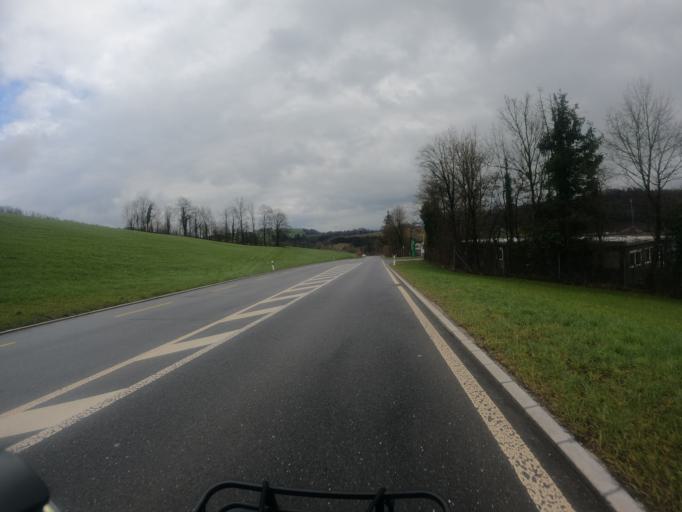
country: CH
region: Zurich
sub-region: Bezirk Affoltern
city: Hausen am Albis / Hausen (Dorf)
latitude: 47.2188
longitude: 8.5613
